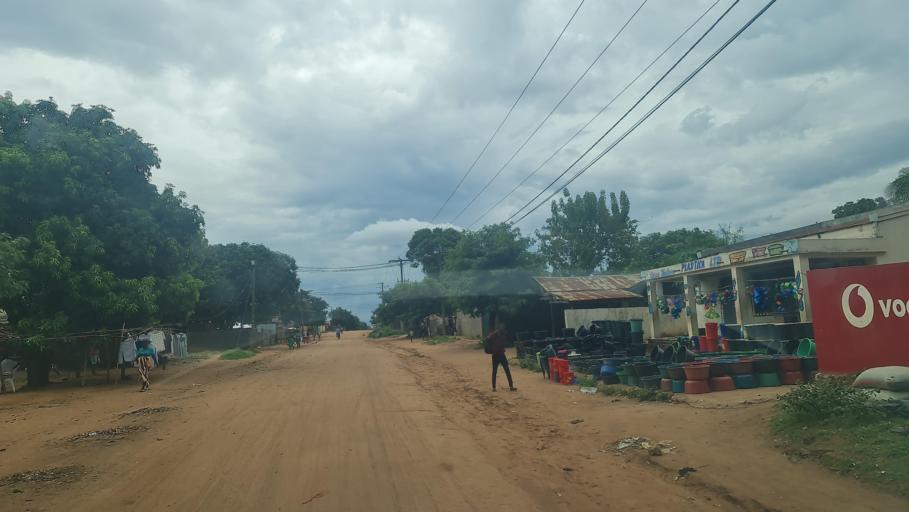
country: MW
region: Southern Region
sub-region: Nsanje District
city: Nsanje
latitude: -17.3317
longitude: 35.5945
